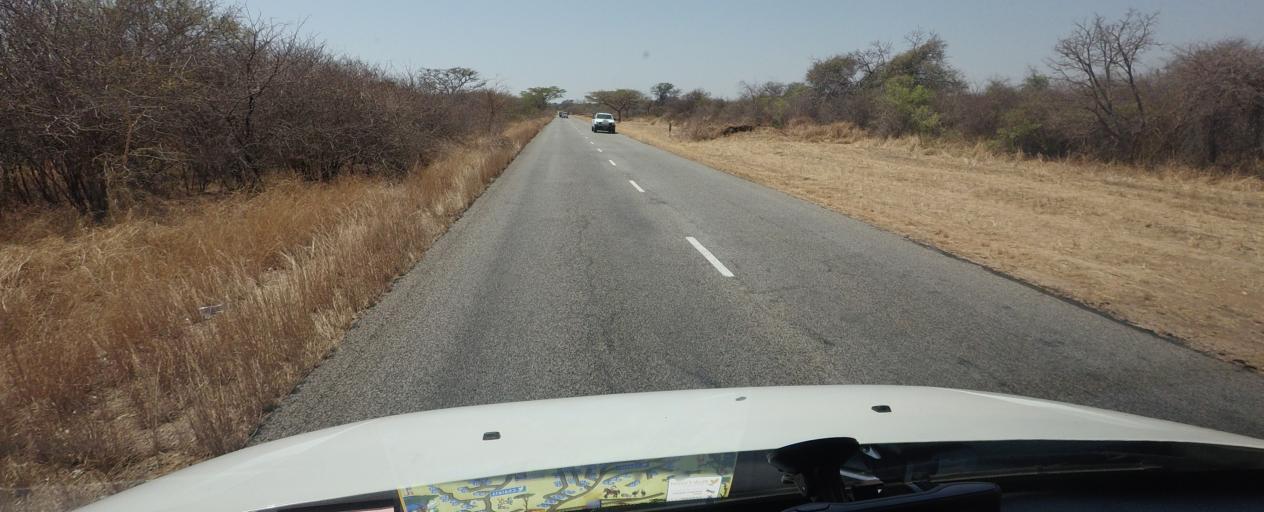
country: ZA
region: Limpopo
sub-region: Mopani District Municipality
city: Hoedspruit
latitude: -24.5291
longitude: 30.9844
